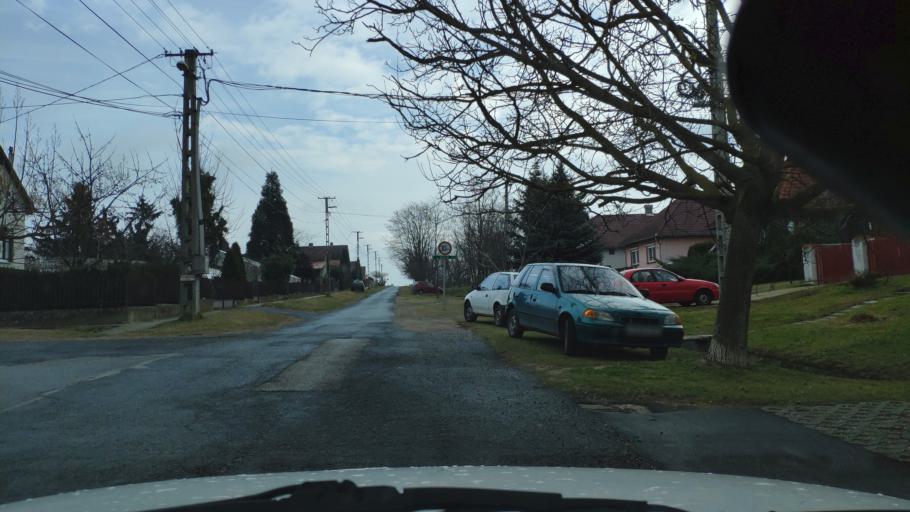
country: HU
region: Zala
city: Nagykanizsa
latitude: 46.4112
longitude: 17.0005
